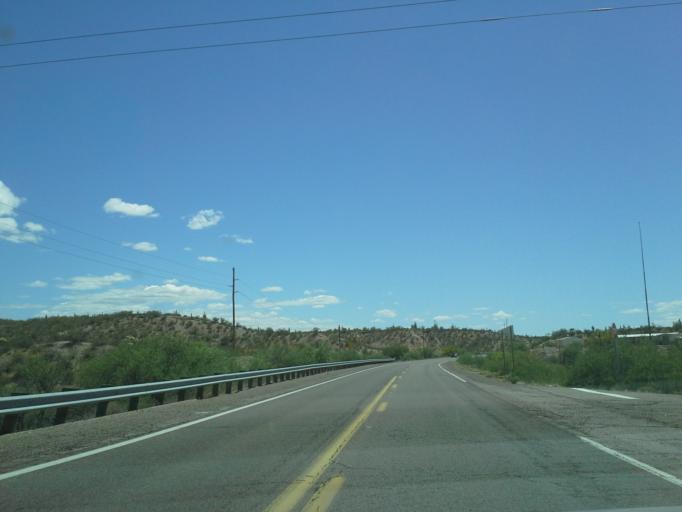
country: US
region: Arizona
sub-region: Pinal County
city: Kearny
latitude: 32.9401
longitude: -110.7388
